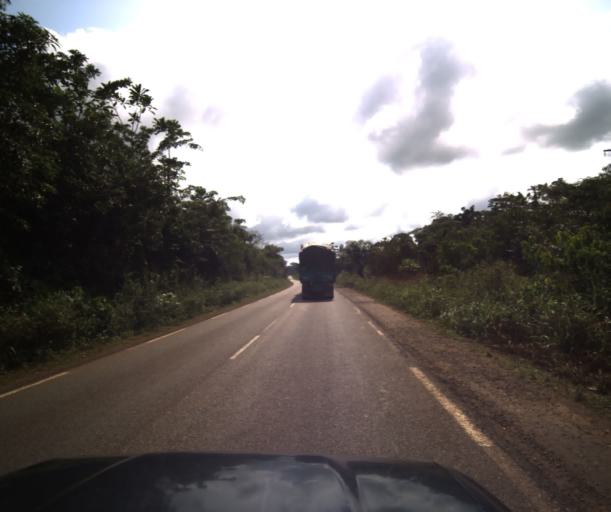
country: CM
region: Littoral
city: Edea
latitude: 3.8027
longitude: 10.2420
